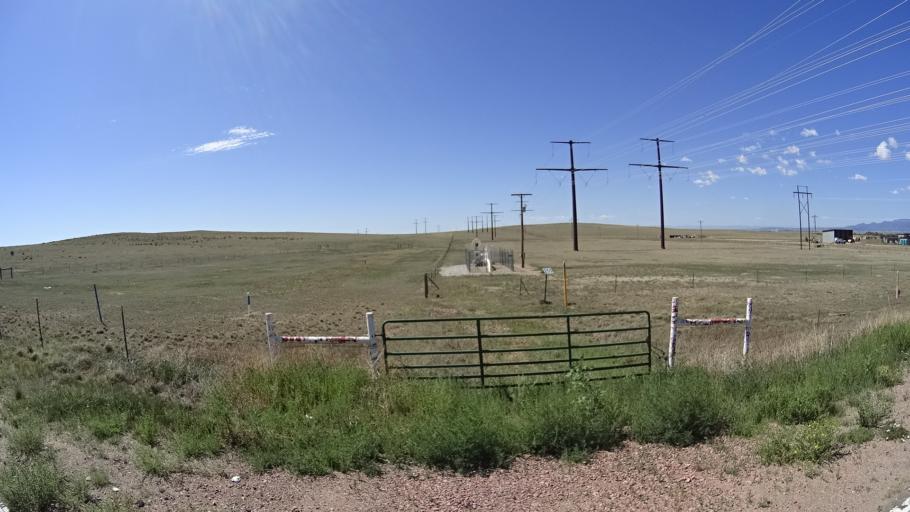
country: US
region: Colorado
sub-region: El Paso County
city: Security-Widefield
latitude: 38.7811
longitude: -104.6273
